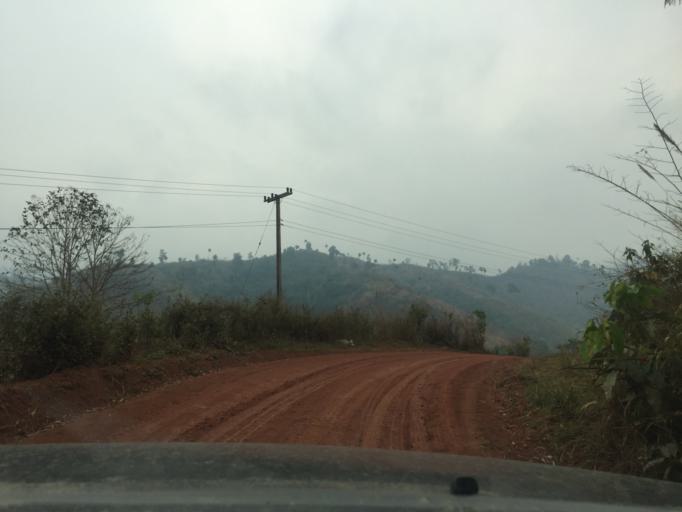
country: TH
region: Nan
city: Bo Kluea
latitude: 18.8415
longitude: 101.4094
